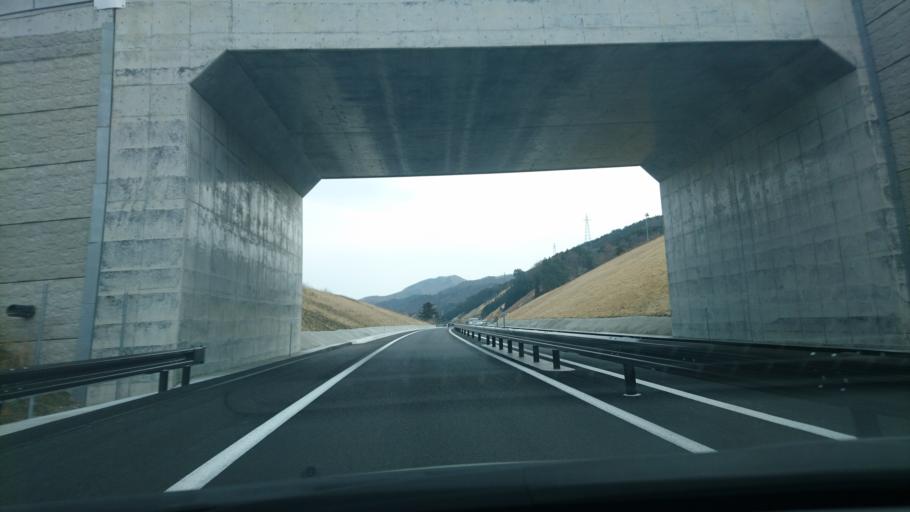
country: JP
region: Iwate
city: Kamaishi
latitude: 39.2514
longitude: 141.7904
